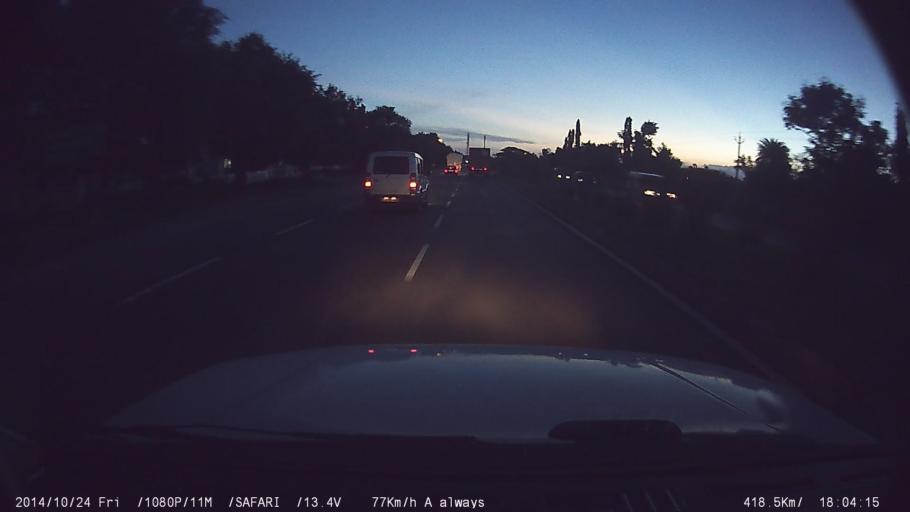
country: IN
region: Tamil Nadu
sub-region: Kancheepuram
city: Chengalpattu
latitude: 12.6118
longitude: 79.9238
